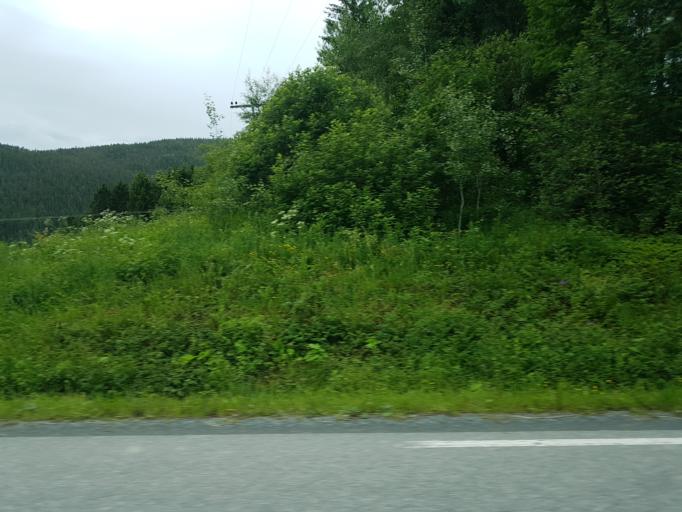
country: NO
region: Nord-Trondelag
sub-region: Levanger
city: Skogn
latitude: 63.6068
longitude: 11.0951
